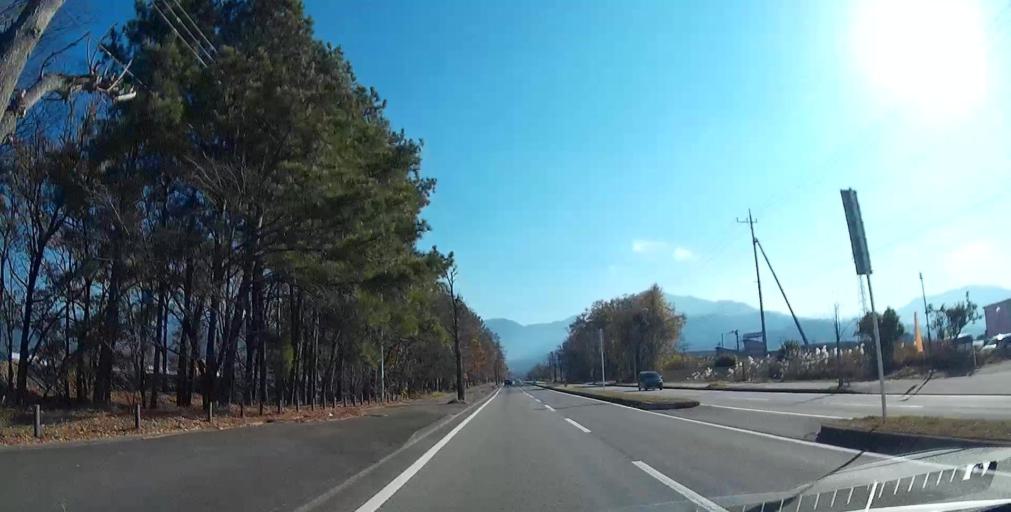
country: JP
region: Yamanashi
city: Isawa
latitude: 35.6301
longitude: 138.6820
